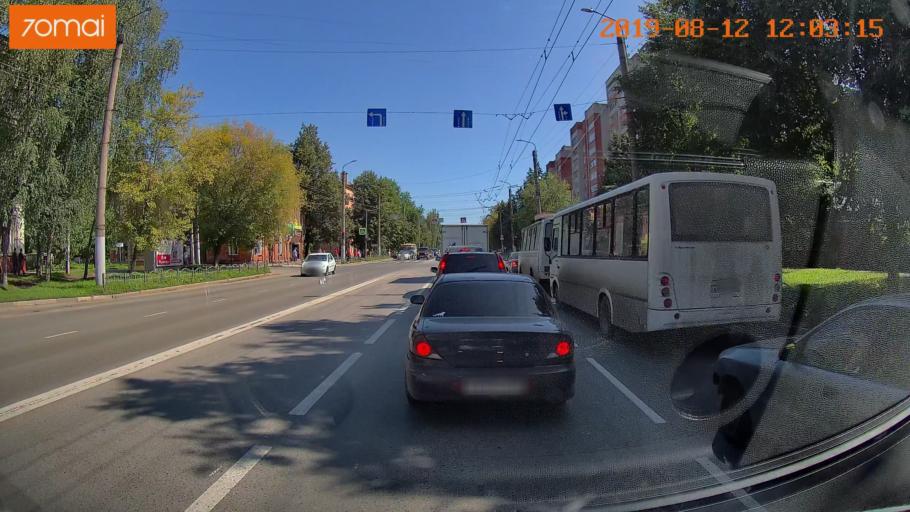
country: RU
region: Ivanovo
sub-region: Gorod Ivanovo
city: Ivanovo
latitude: 56.9946
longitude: 40.9998
